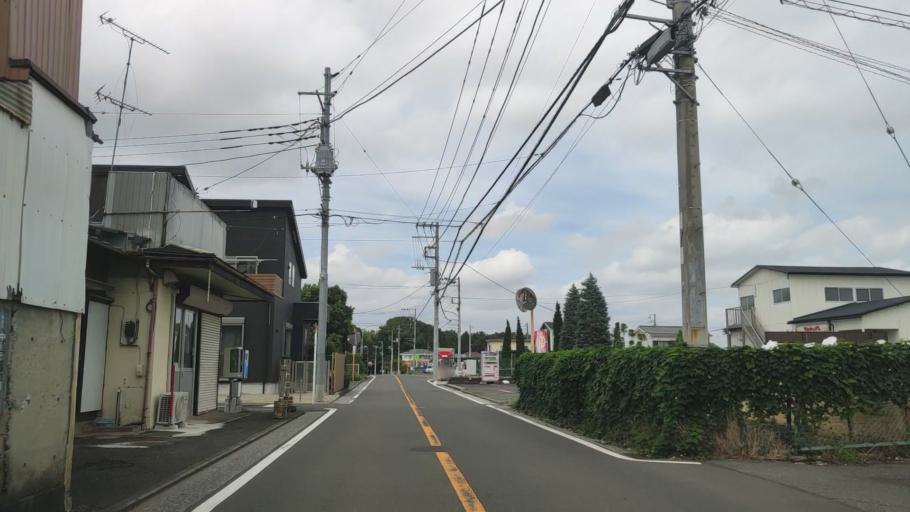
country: JP
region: Kanagawa
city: Minami-rinkan
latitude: 35.4814
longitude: 139.4752
